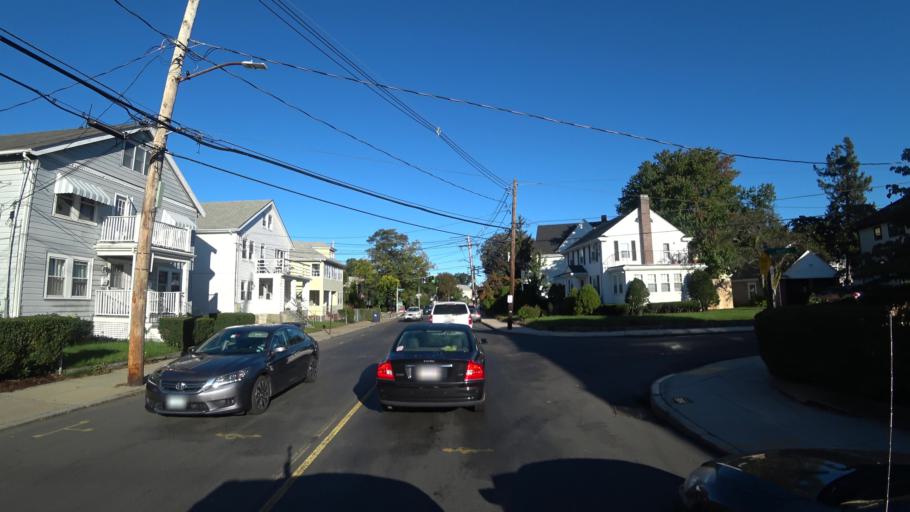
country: US
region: Massachusetts
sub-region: Middlesex County
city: Watertown
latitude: 42.3549
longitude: -71.1556
